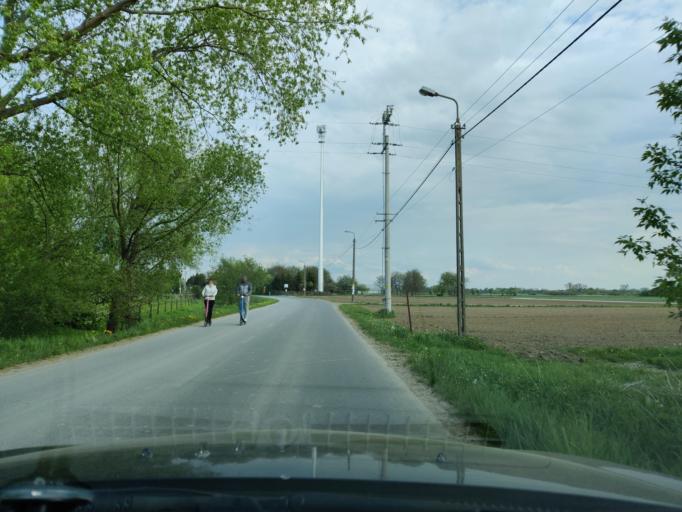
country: PL
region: Masovian Voivodeship
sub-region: Powiat piaseczynski
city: Konstancin-Jeziorna
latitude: 52.1270
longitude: 21.1393
